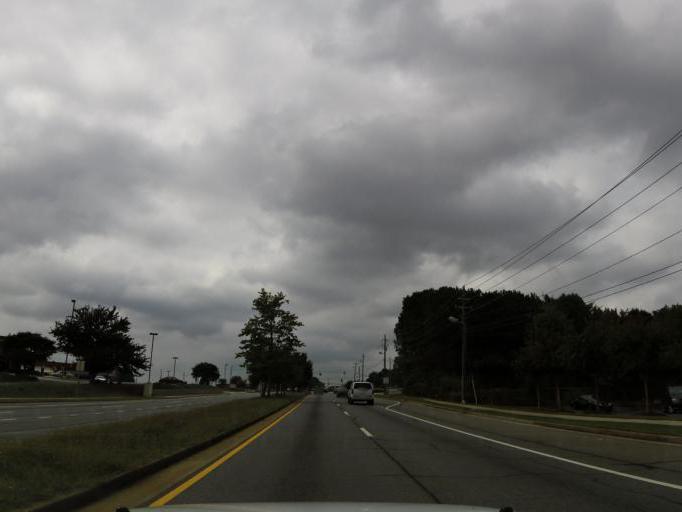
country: US
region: Georgia
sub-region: Cobb County
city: Austell
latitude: 33.8668
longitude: -84.6278
